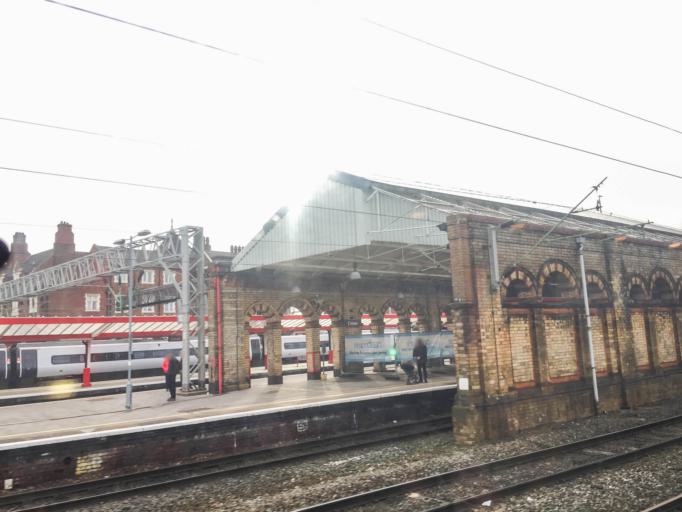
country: GB
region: England
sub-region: Cheshire East
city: Crewe
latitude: 53.0903
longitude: -2.4340
